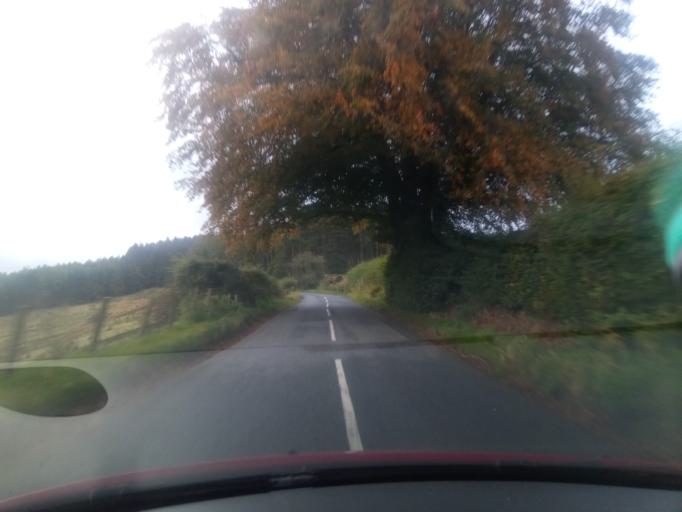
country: GB
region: Scotland
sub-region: The Scottish Borders
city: Hawick
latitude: 55.3399
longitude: -2.6517
